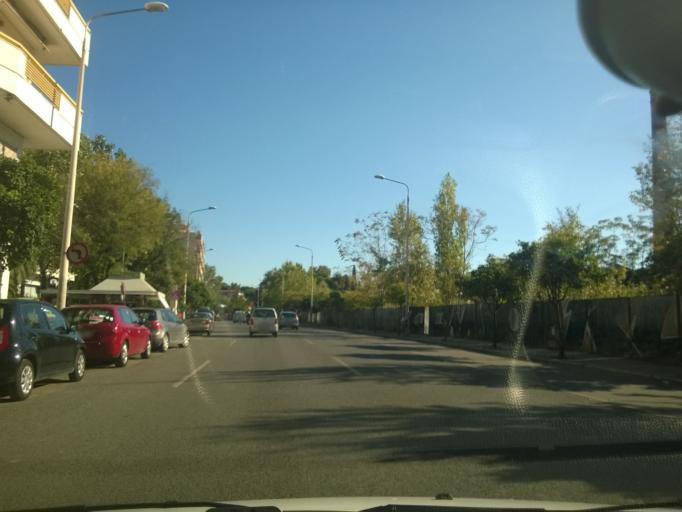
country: GR
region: Central Macedonia
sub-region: Nomos Thessalonikis
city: Kalamaria
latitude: 40.5969
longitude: 22.9528
